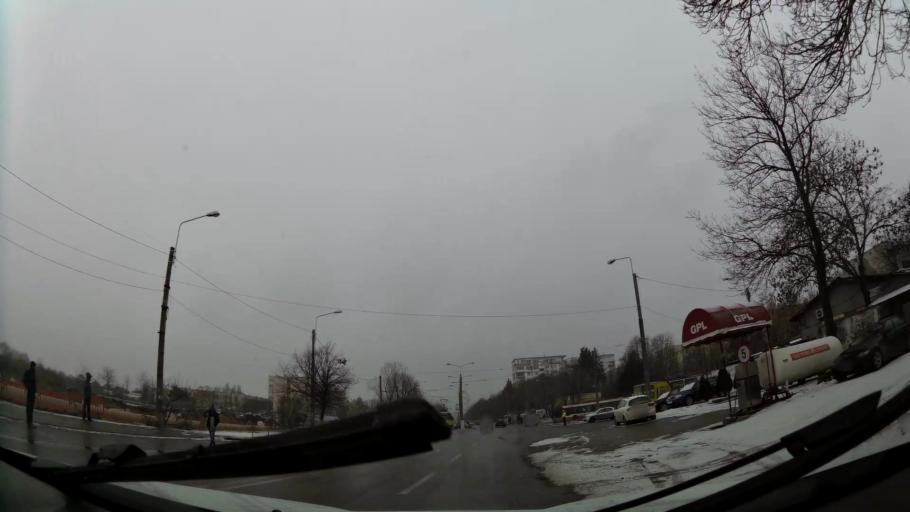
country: RO
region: Prahova
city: Ploiesti
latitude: 44.9640
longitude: 26.0064
